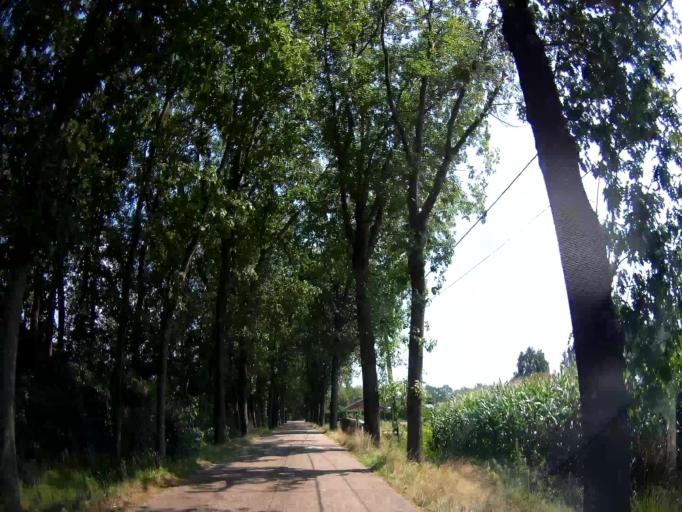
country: BE
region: Flanders
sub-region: Provincie Antwerpen
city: Oud-Turnhout
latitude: 51.2893
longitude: 5.0014
